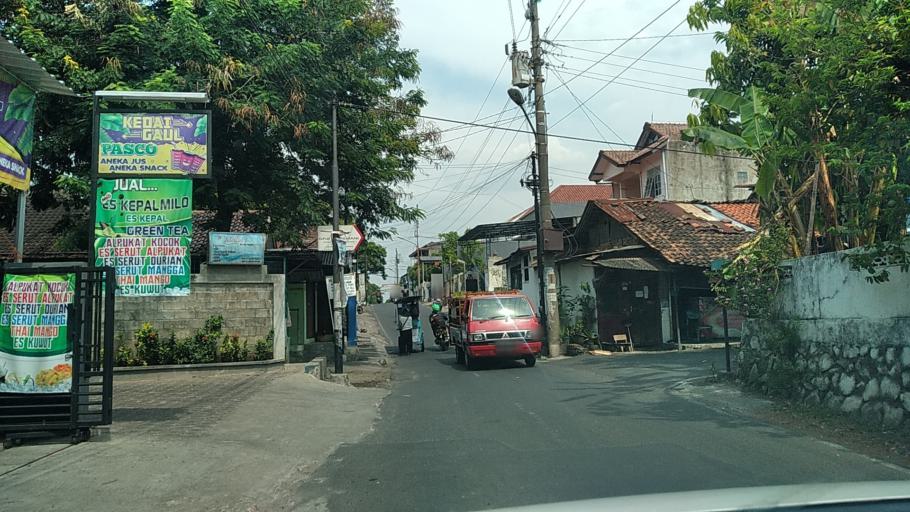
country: ID
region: Central Java
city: Semarang
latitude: -7.0325
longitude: 110.4223
